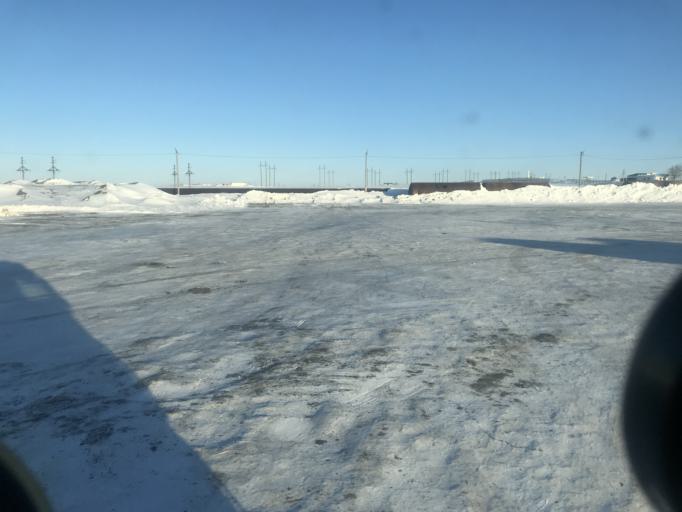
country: KZ
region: Aqtoebe
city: Khromtau
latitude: 50.2532
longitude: 58.4135
